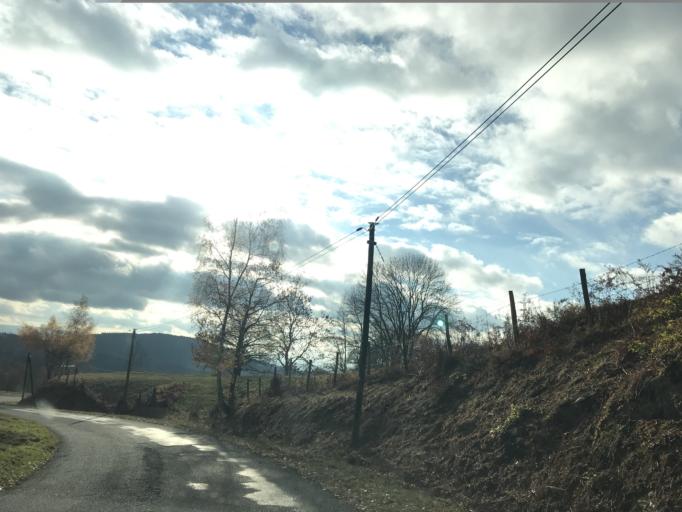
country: FR
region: Auvergne
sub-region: Departement du Puy-de-Dome
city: Celles-sur-Durolle
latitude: 45.7750
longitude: 3.6666
